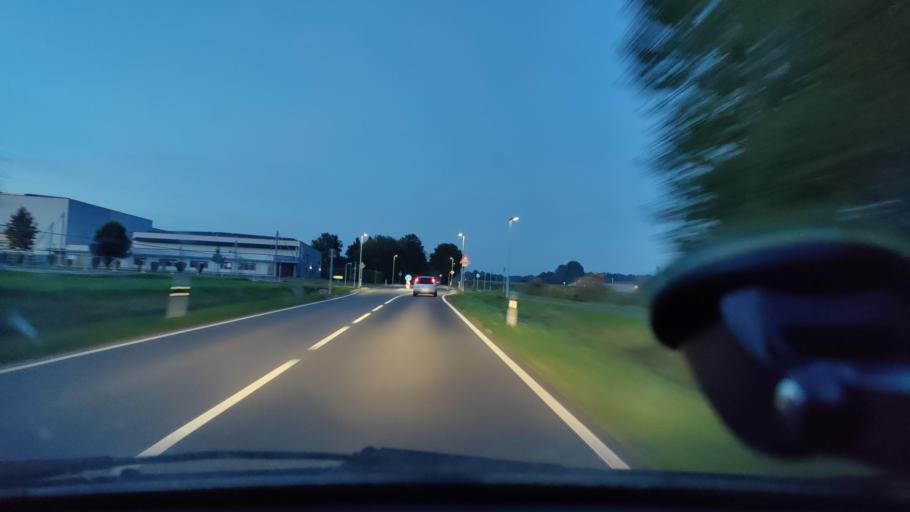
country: DE
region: North Rhine-Westphalia
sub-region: Regierungsbezirk Munster
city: Sudlohn
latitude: 51.9059
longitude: 6.8656
